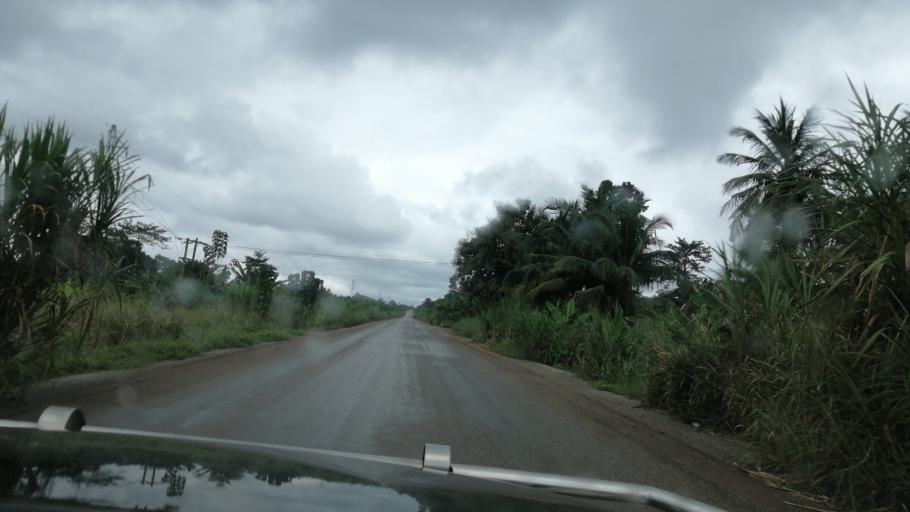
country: GH
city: Duayaw Nkwanta
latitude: 6.9016
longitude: -2.4012
